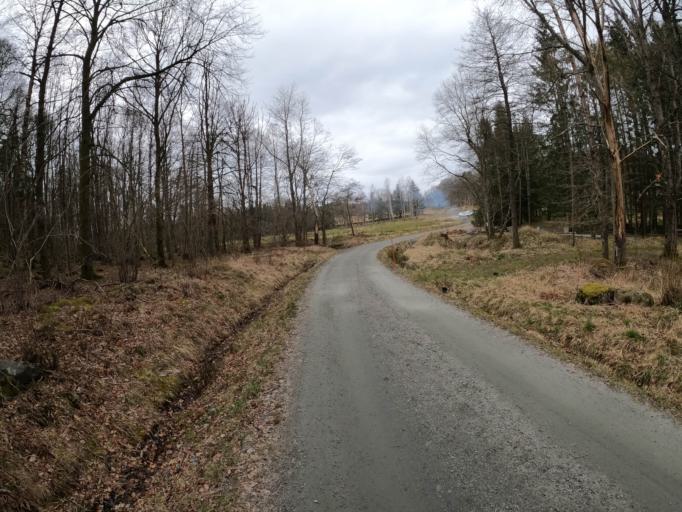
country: SE
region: Vaestra Goetaland
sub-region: Harryda Kommun
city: Molnlycke
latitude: 57.6260
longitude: 12.1075
